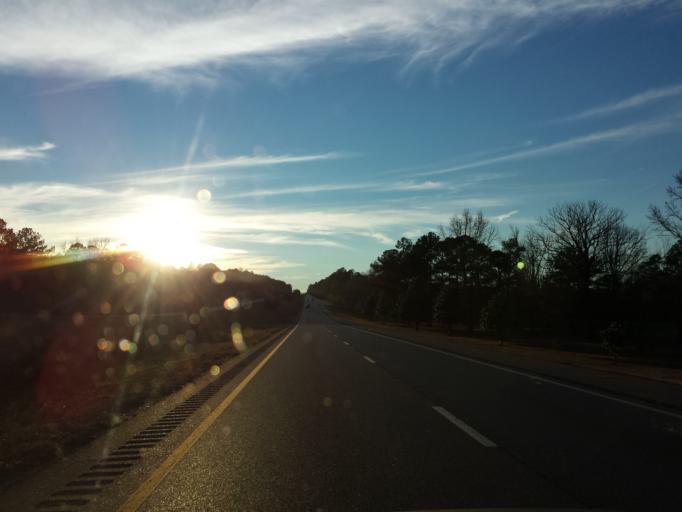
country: US
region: Mississippi
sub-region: Lauderdale County
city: Marion
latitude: 32.4100
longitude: -88.5339
